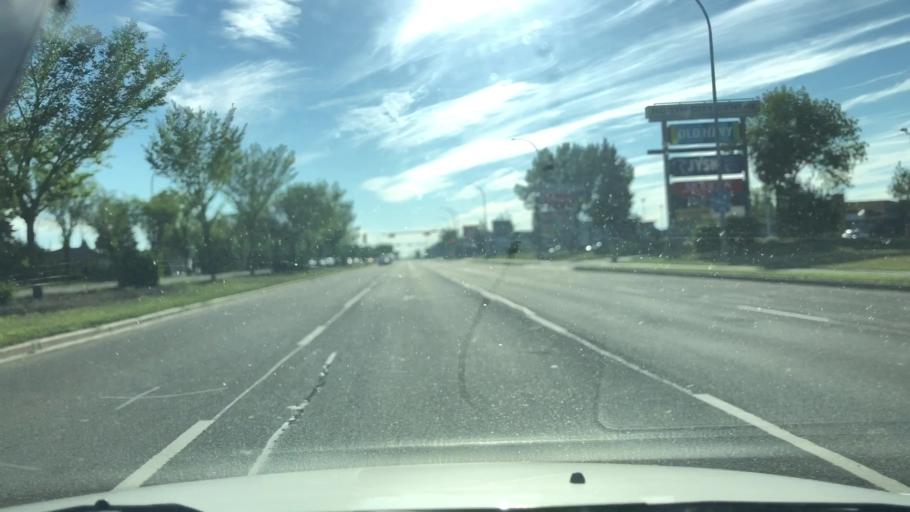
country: CA
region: Alberta
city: Edmonton
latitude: 53.5996
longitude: -113.5481
